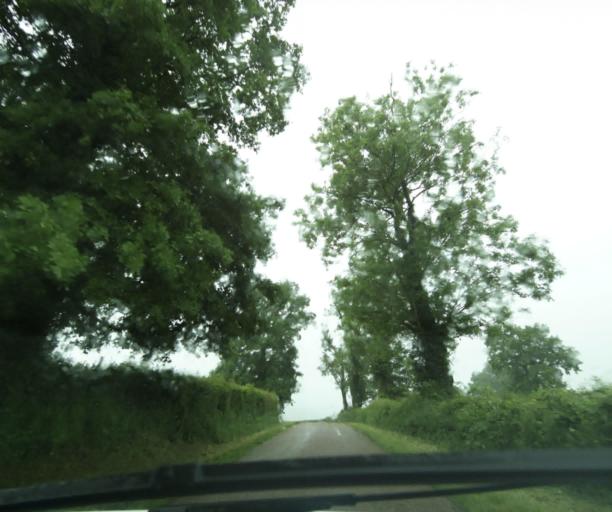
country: FR
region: Bourgogne
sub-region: Departement de Saone-et-Loire
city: Charolles
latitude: 46.3840
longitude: 4.2944
